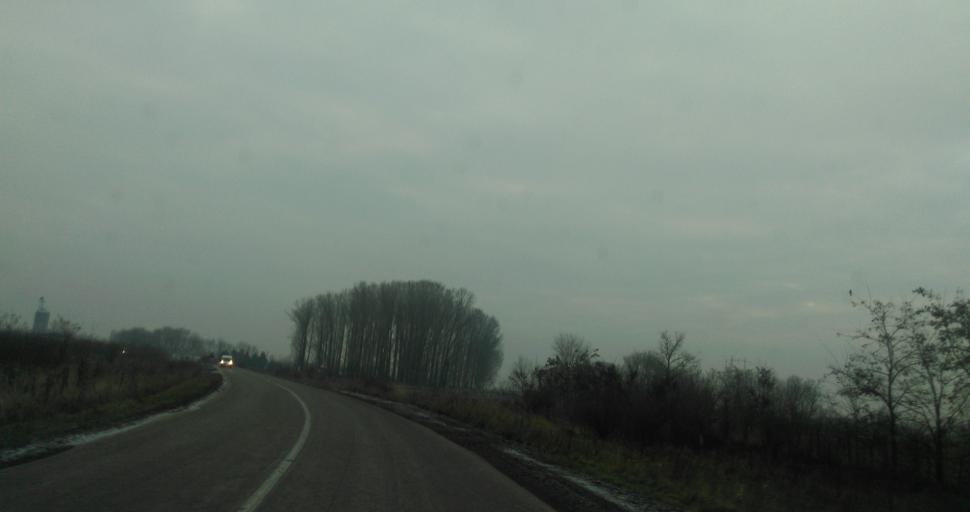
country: RS
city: Kumane
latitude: 45.5395
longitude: 20.2107
